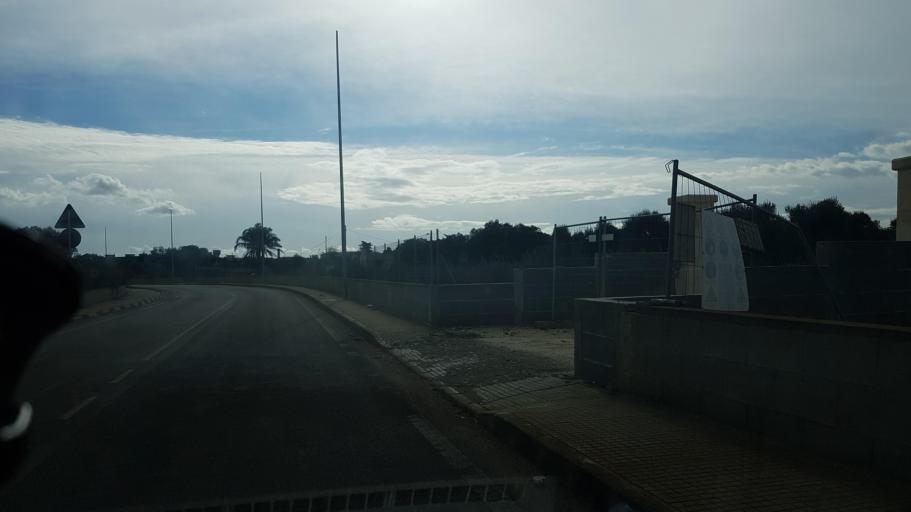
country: IT
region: Apulia
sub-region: Provincia di Brindisi
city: San Vito dei Normanni
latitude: 40.6629
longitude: 17.7145
